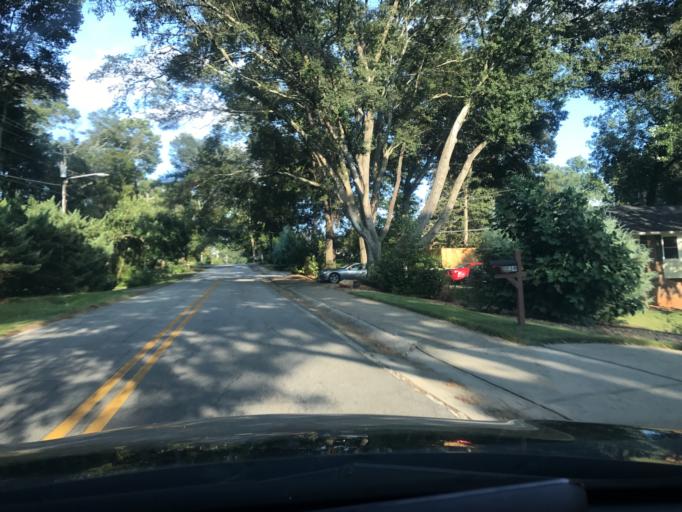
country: US
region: Georgia
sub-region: DeKalb County
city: Clarkston
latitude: 33.8243
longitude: -84.2689
